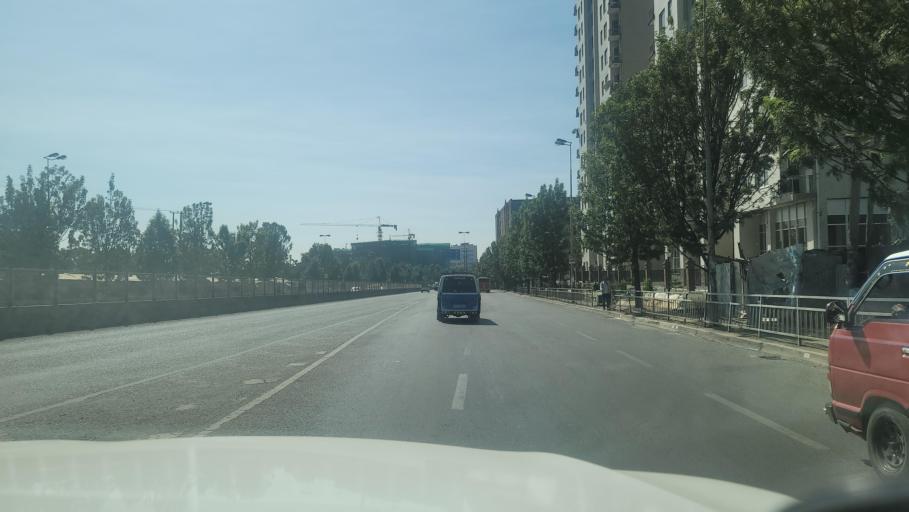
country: ET
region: Adis Abeba
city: Addis Ababa
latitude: 9.0155
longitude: 38.8028
